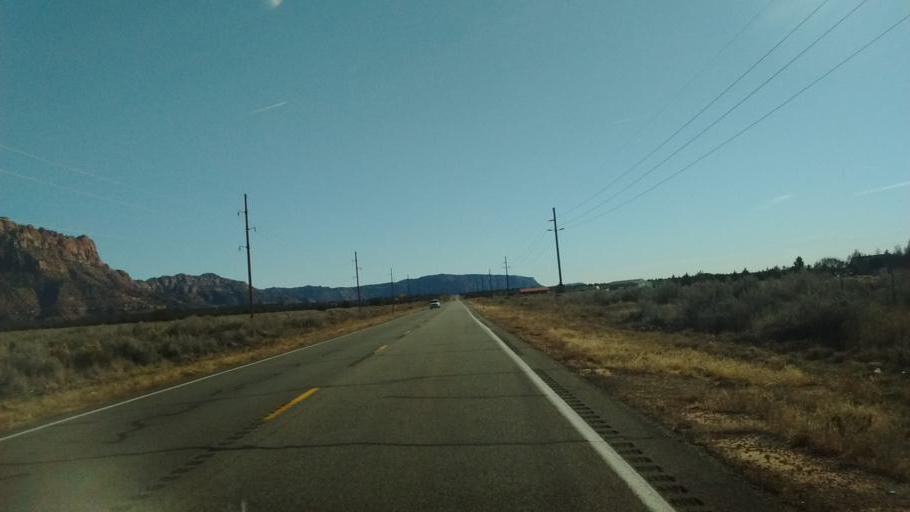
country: US
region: Arizona
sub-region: Mohave County
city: Colorado City
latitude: 37.0292
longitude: -113.0537
